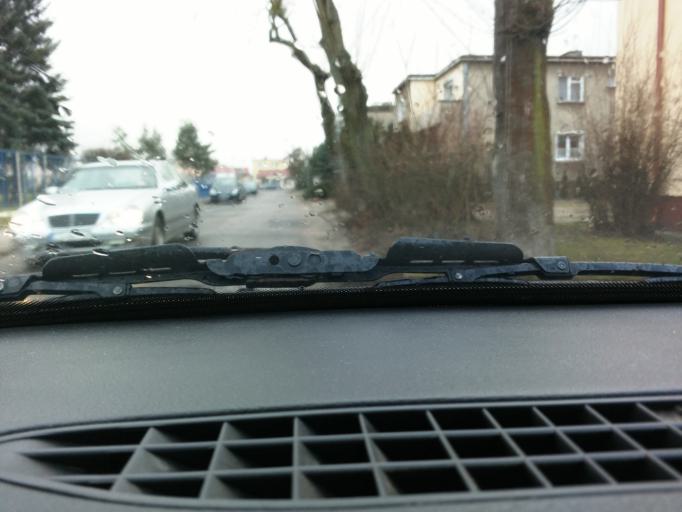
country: PL
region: Kujawsko-Pomorskie
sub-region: Grudziadz
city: Grudziadz
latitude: 53.4288
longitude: 18.7267
